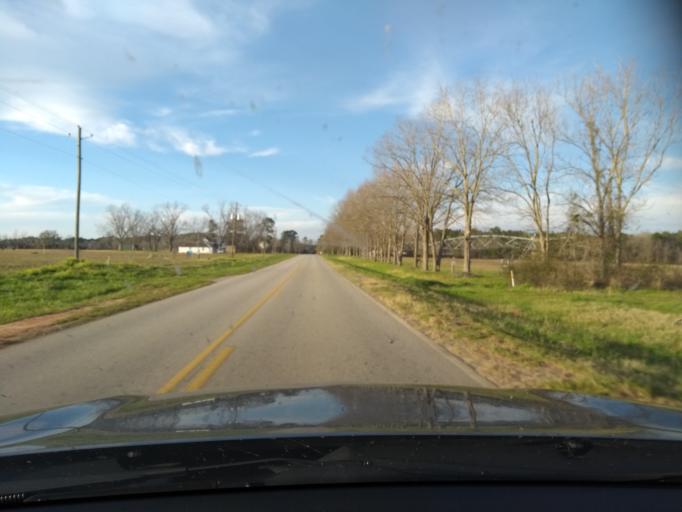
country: US
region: Georgia
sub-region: Bulloch County
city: Statesboro
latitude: 32.3363
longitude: -81.7735
